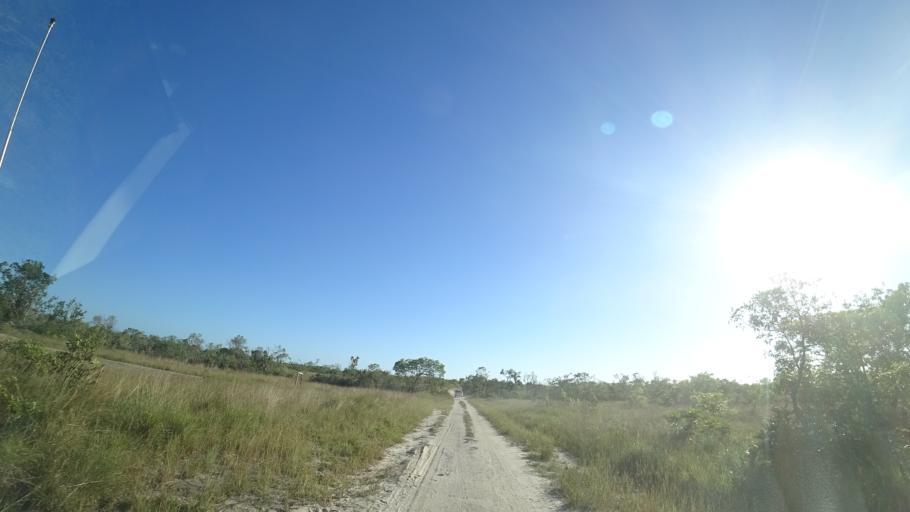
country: MZ
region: Sofala
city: Beira
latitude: -19.5739
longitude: 35.2258
